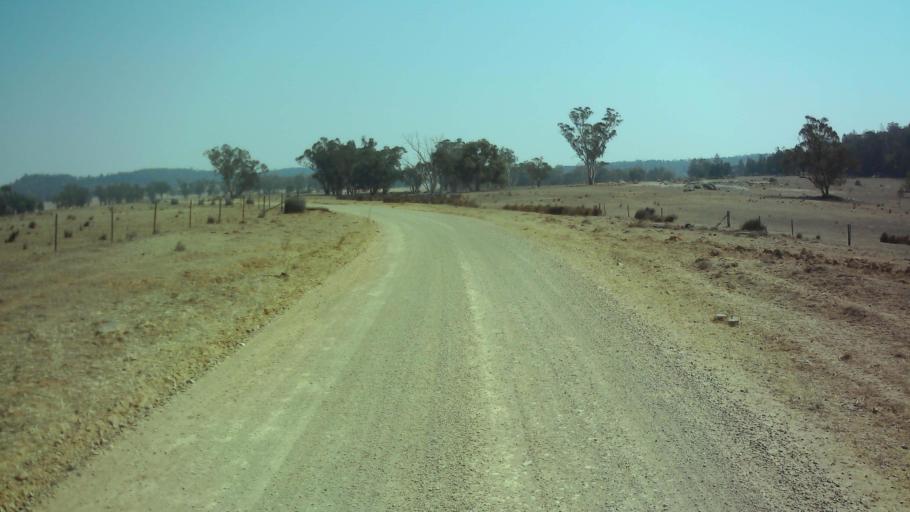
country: AU
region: New South Wales
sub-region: Weddin
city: Grenfell
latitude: -33.6785
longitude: 148.2767
